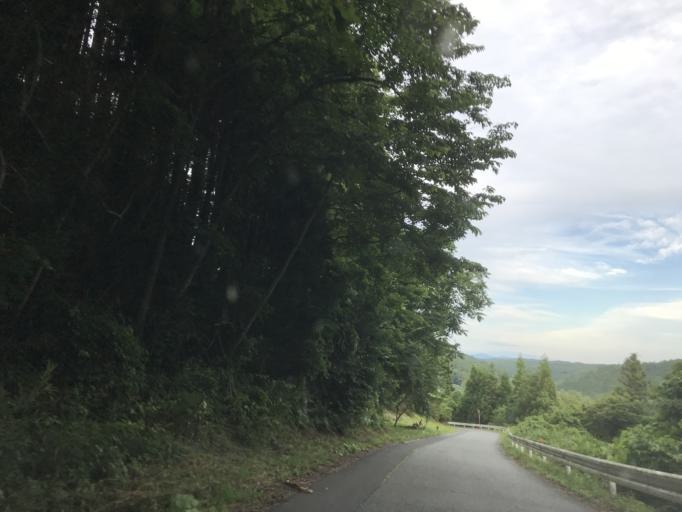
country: JP
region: Iwate
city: Ichinoseki
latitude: 38.9127
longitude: 141.0440
